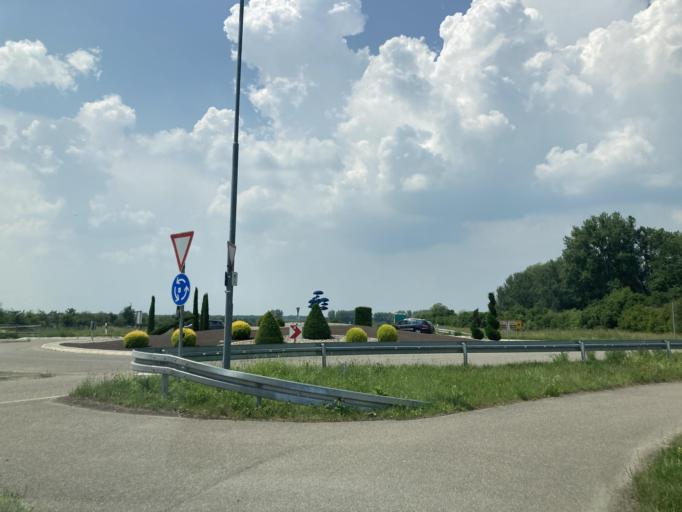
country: DE
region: Baden-Wuerttemberg
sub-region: Karlsruhe Region
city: Linkenheim-Hochstetten
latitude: 49.1536
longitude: 8.4125
